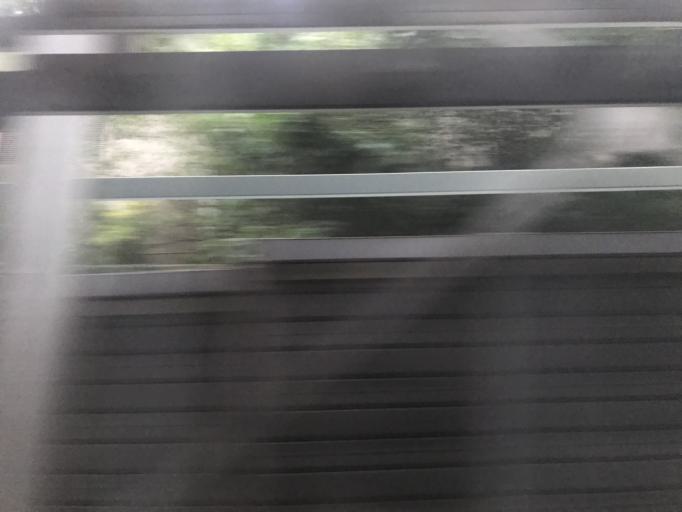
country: HK
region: Sha Tin
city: Sha Tin
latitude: 22.3690
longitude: 114.1733
